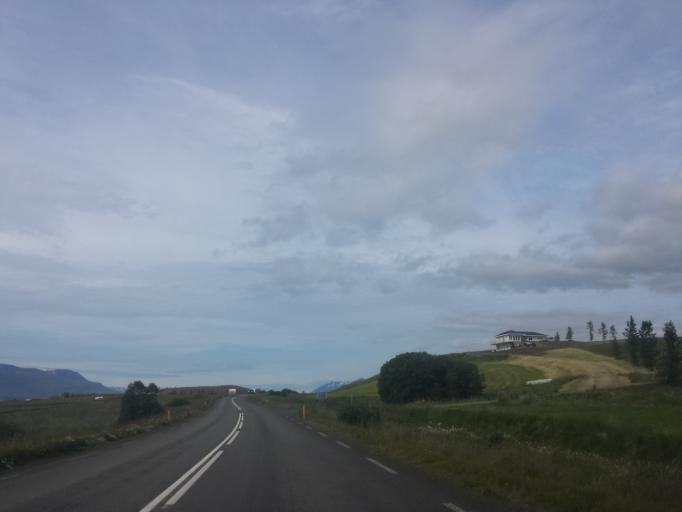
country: IS
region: Northeast
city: Akureyri
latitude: 65.7144
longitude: -18.0676
